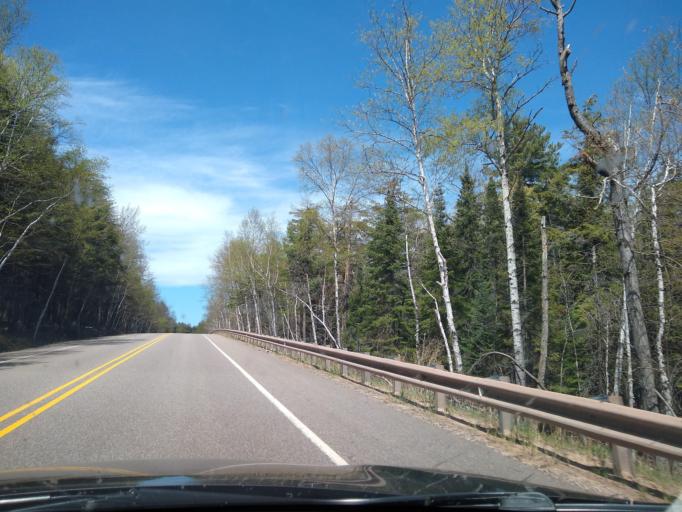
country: US
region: Michigan
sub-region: Marquette County
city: Trowbridge Park
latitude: 46.6202
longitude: -87.4673
